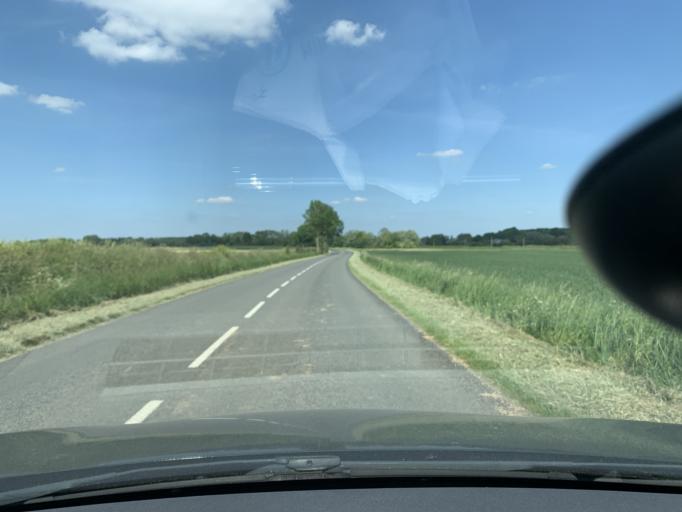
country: FR
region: Nord-Pas-de-Calais
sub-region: Departement du Pas-de-Calais
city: Marquion
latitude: 50.2302
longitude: 3.0862
